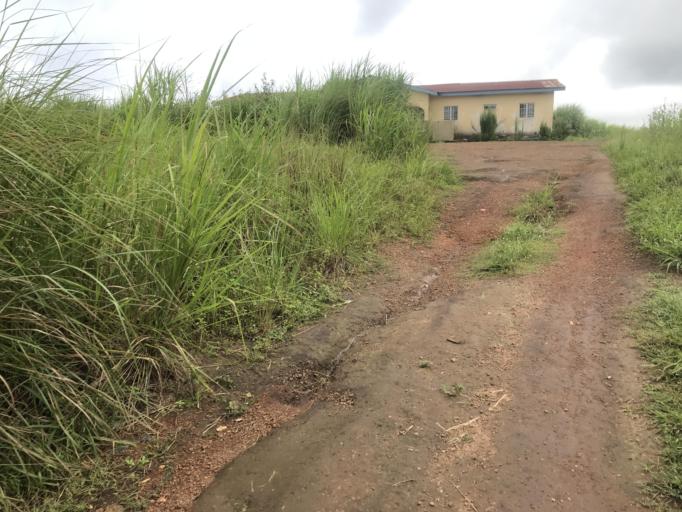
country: SL
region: Eastern Province
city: Buedu
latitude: 8.4620
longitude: -10.3271
